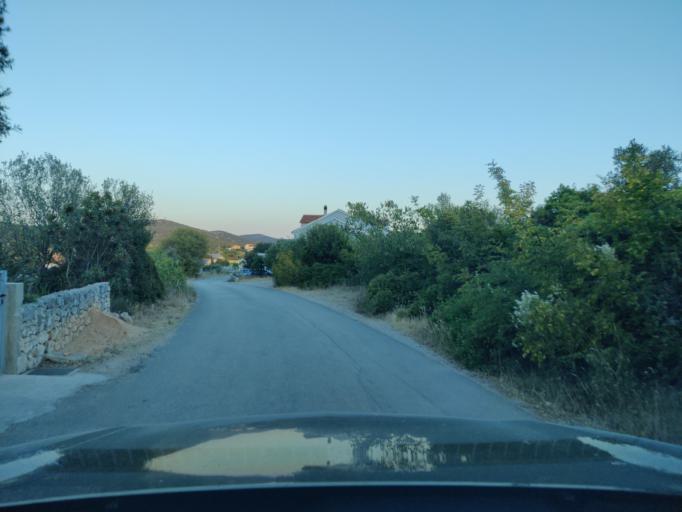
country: HR
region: Sibensko-Kniniska
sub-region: Grad Sibenik
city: Tisno
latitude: 43.8057
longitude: 15.6455
